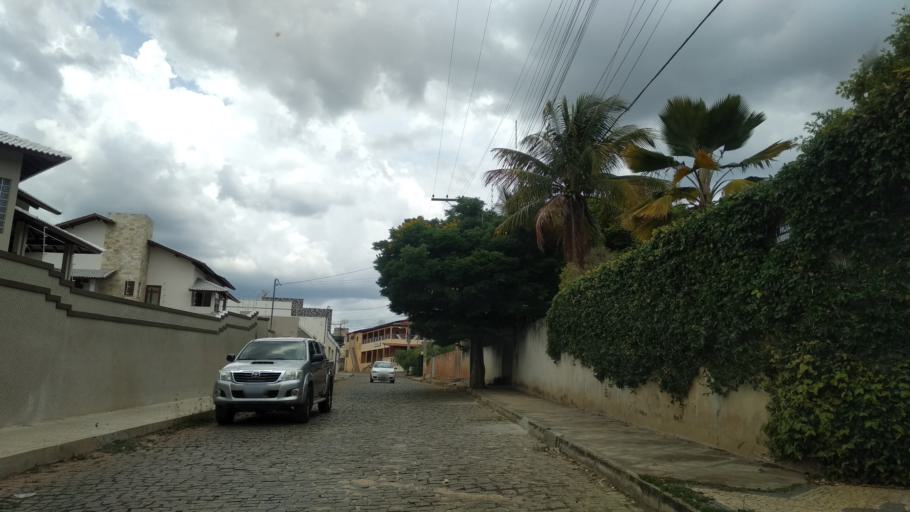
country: BR
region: Bahia
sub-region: Caetite
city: Caetite
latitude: -14.0709
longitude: -42.4815
